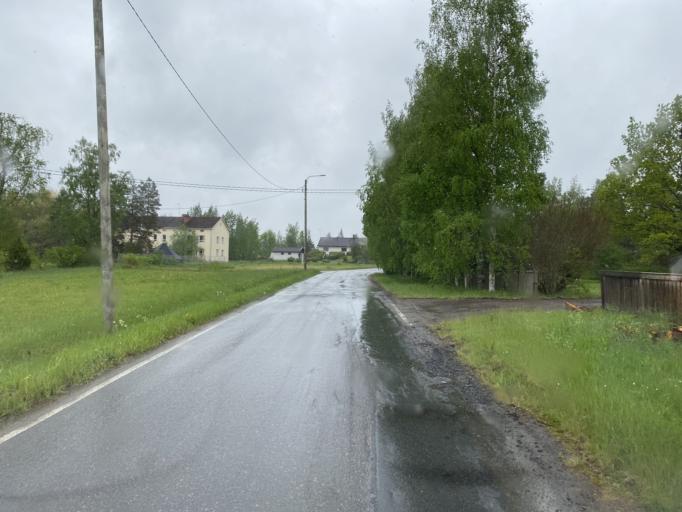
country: FI
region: Haeme
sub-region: Forssa
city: Humppila
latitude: 61.0970
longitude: 23.3165
